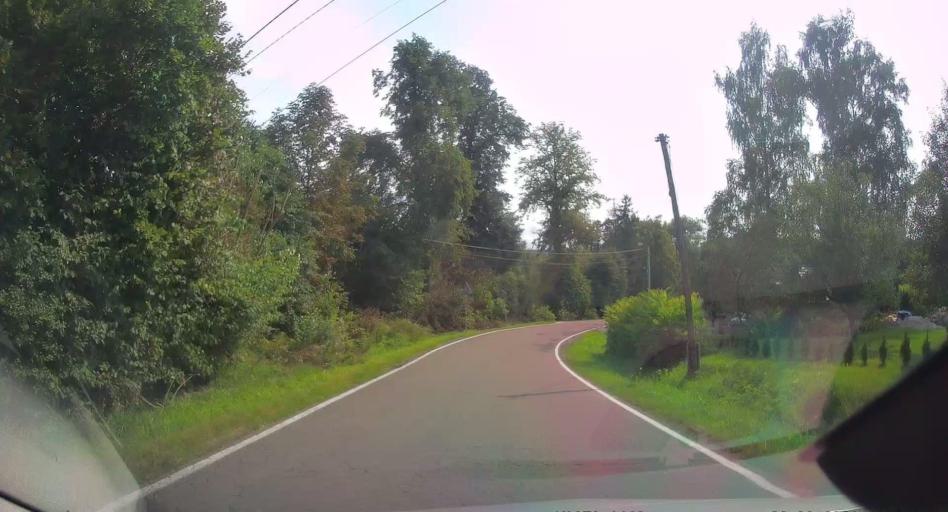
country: PL
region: Lesser Poland Voivodeship
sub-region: Powiat wielicki
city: Pawlikowice
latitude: 49.9529
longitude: 20.0430
